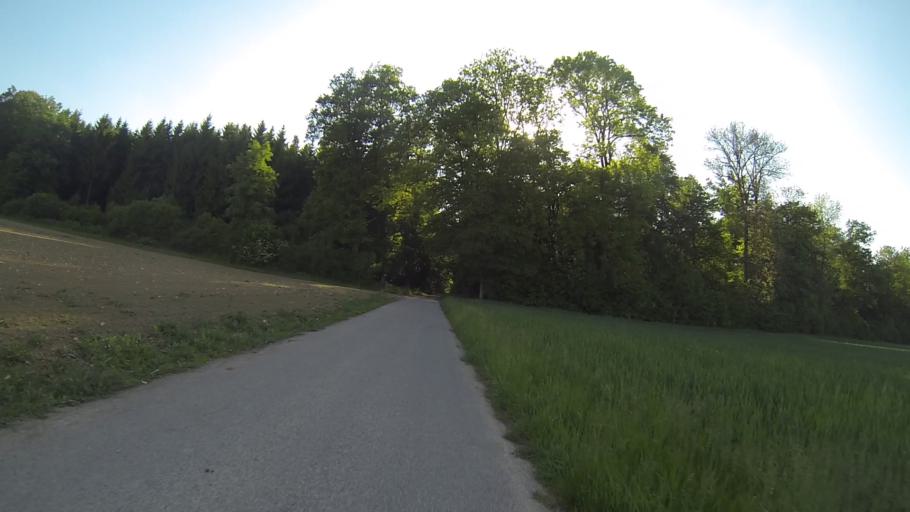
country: DE
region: Baden-Wuerttemberg
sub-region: Tuebingen Region
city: Ollingen
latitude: 48.5425
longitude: 10.1641
